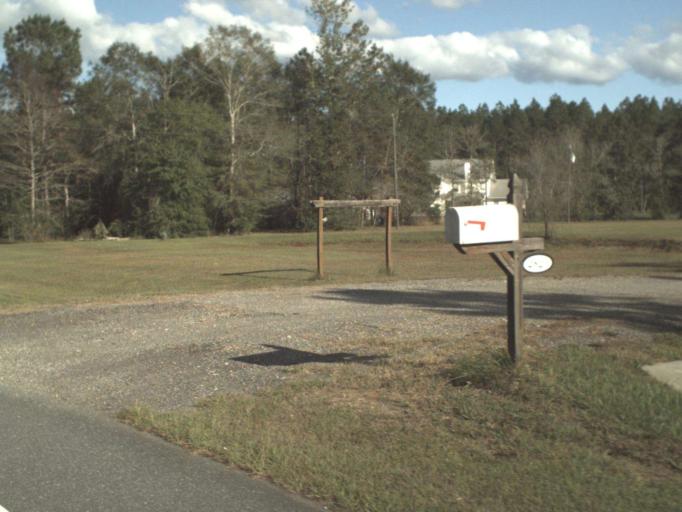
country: US
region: Florida
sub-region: Holmes County
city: Bonifay
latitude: 30.6603
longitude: -85.6538
